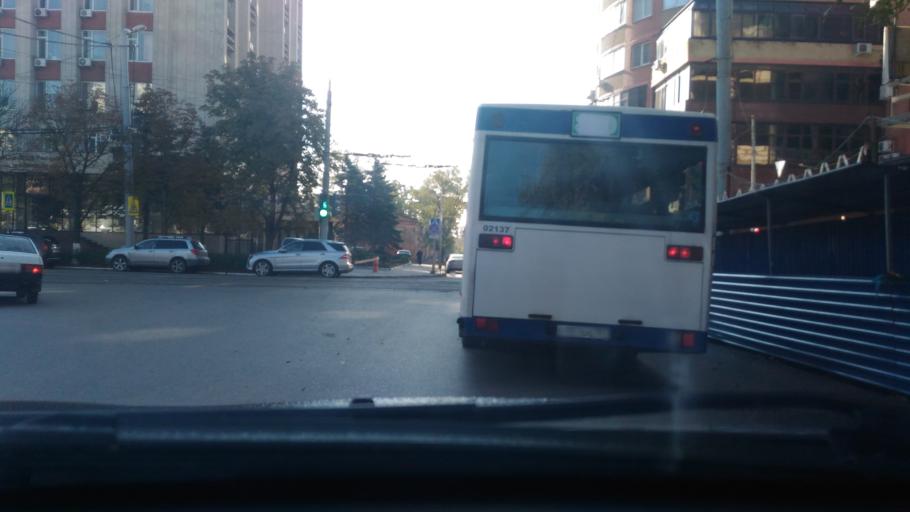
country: RU
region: Rostov
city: Rostov-na-Donu
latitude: 47.2291
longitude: 39.7628
